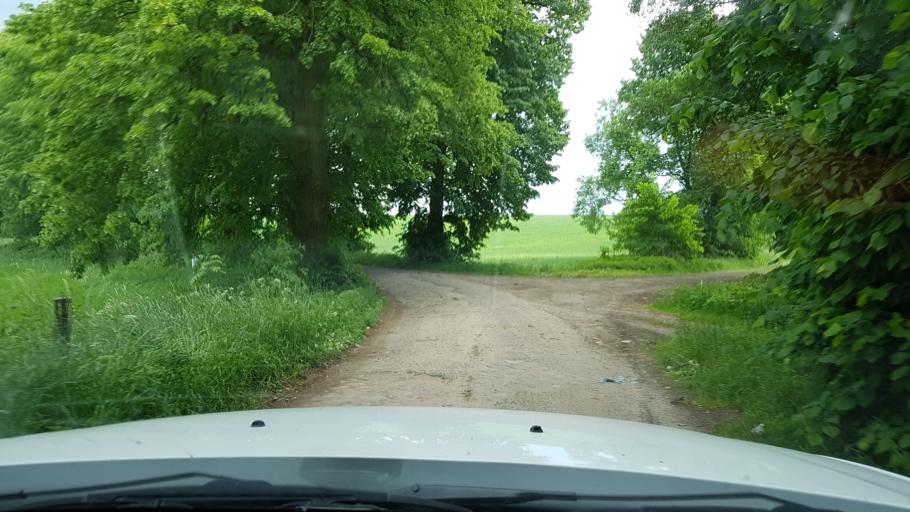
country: PL
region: West Pomeranian Voivodeship
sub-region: Powiat stargardzki
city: Stara Dabrowa
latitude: 53.3793
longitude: 15.1672
